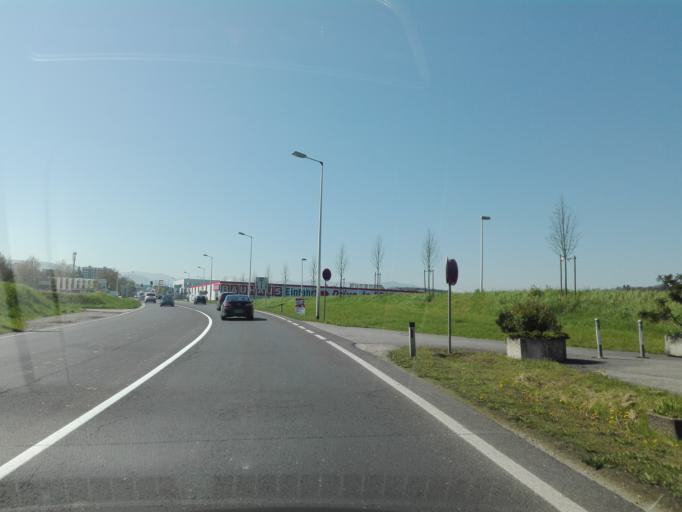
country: AT
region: Upper Austria
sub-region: Steyr Stadt
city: Steyr
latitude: 48.0662
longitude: 14.4213
